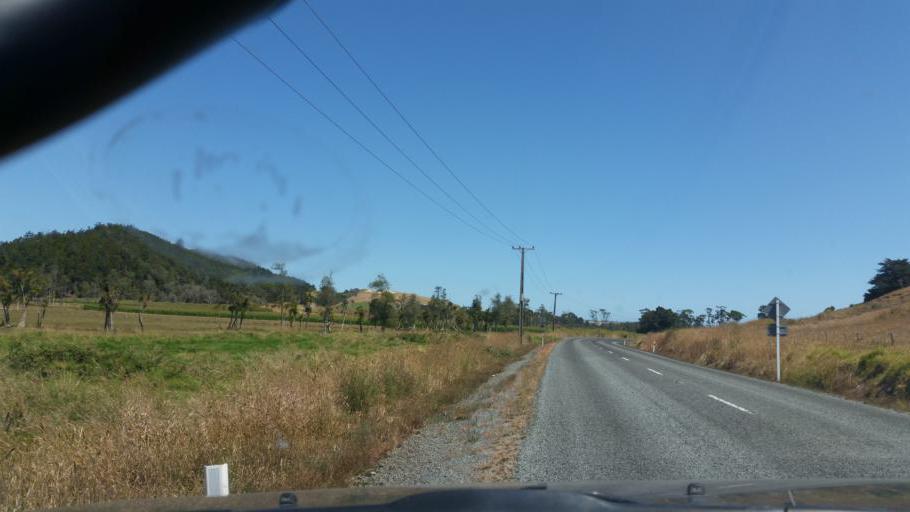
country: NZ
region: Northland
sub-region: Kaipara District
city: Dargaville
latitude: -36.0052
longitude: 173.9625
